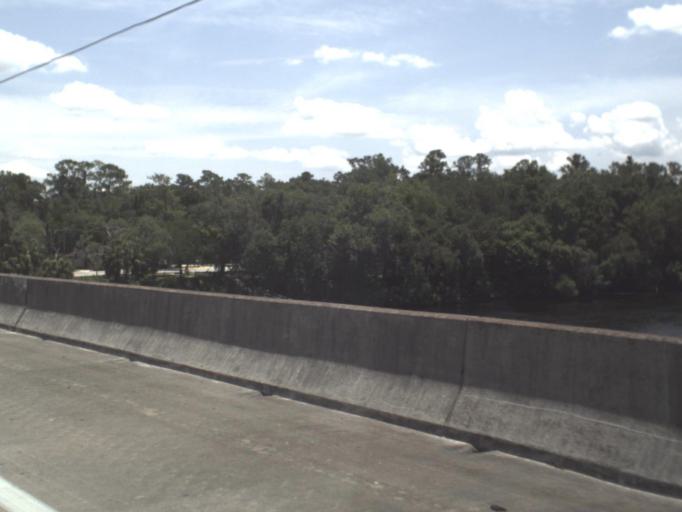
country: US
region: Florida
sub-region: Levy County
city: Manatee Road
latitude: 29.5912
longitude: -82.9380
